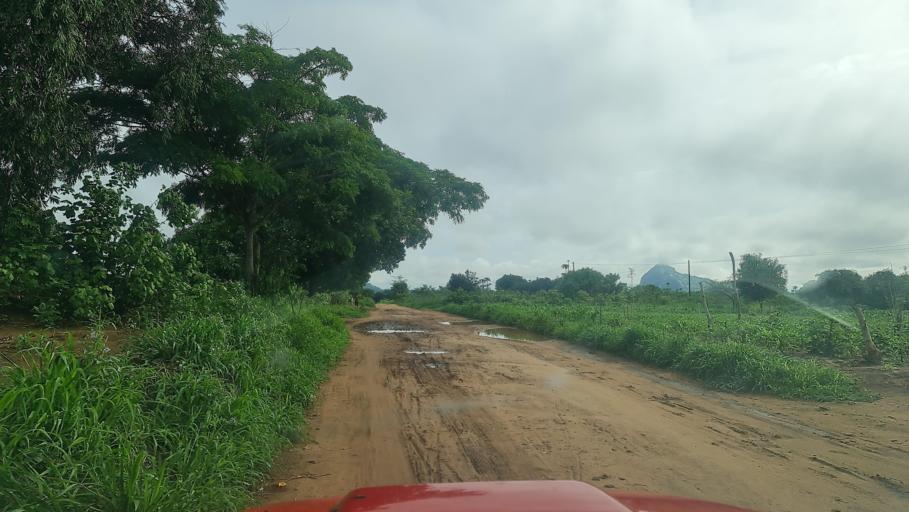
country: MW
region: Southern Region
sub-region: Nsanje District
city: Nsanje
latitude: -17.2830
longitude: 35.6127
